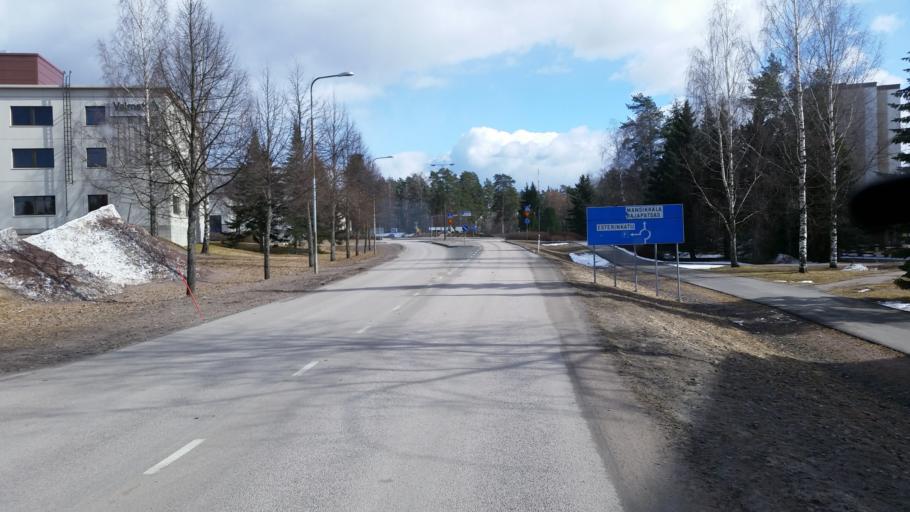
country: FI
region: South Karelia
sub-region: Imatra
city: Imatra
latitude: 61.1699
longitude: 28.7624
